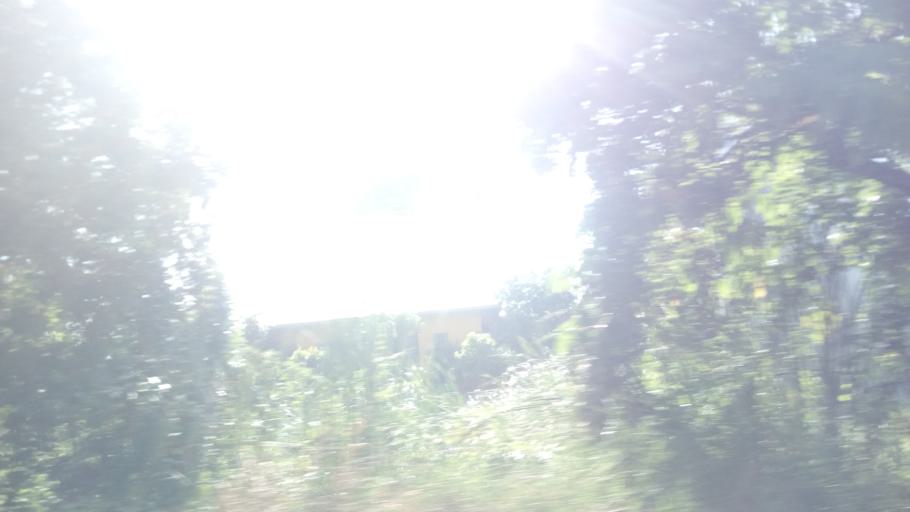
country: TH
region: Nakhon Pathom
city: Salaya
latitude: 13.8155
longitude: 100.3090
